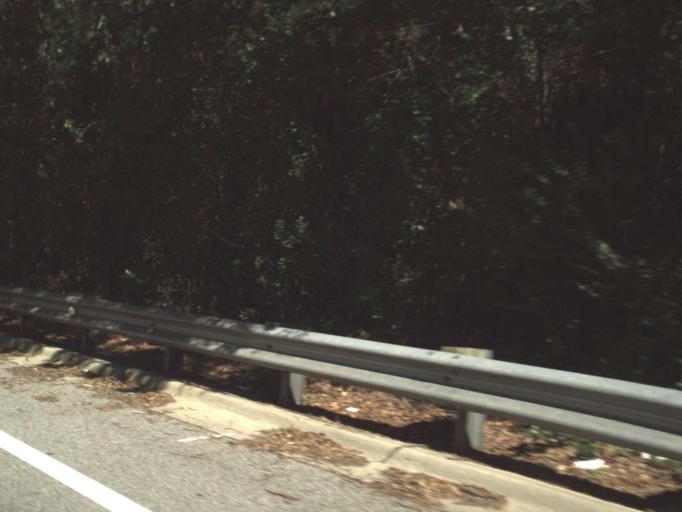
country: US
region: Florida
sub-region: Escambia County
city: Ferry Pass
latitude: 30.4920
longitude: -87.1559
